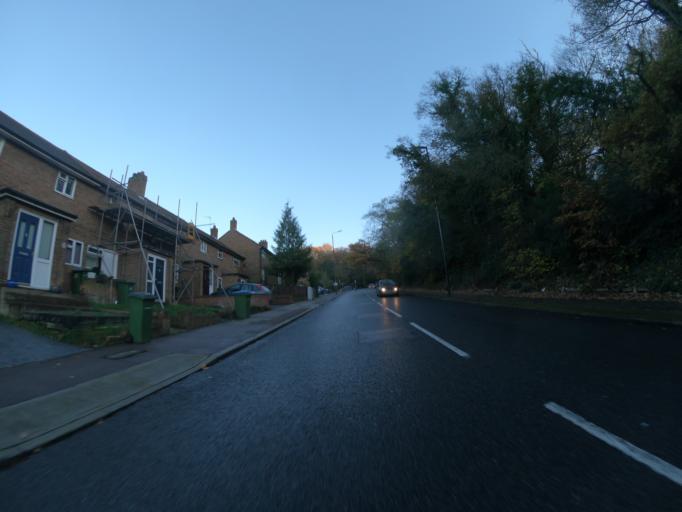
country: GB
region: England
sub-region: Greater London
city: Abbey Wood
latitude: 51.4840
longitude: 0.1090
